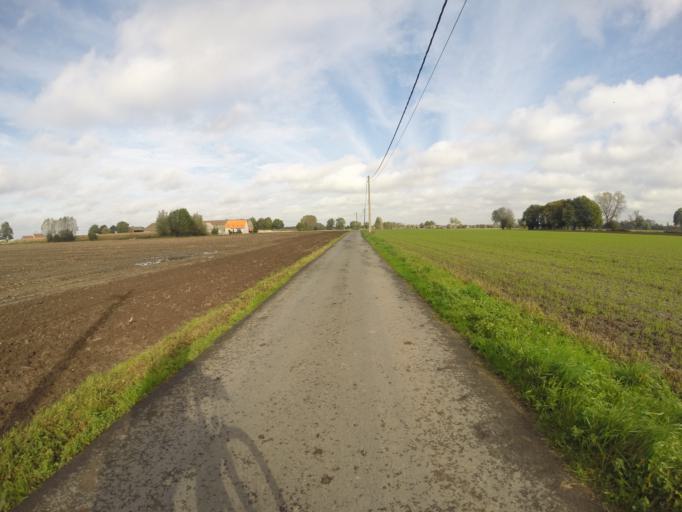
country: BE
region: Flanders
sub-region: Provincie Oost-Vlaanderen
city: Knesselare
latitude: 51.1081
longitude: 3.4179
